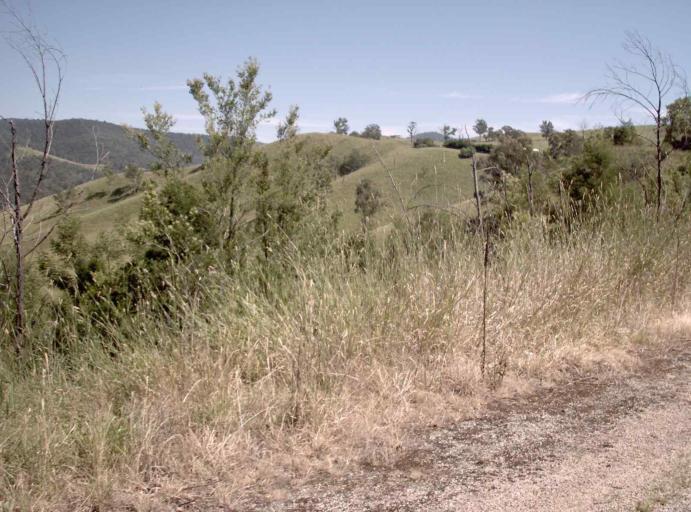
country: AU
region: Victoria
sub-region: East Gippsland
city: Lakes Entrance
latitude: -37.4874
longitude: 148.1868
